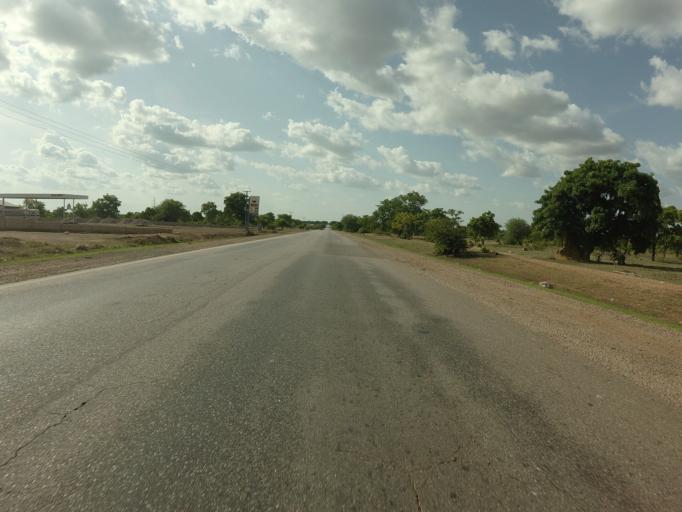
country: GH
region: Upper East
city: Bolgatanga
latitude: 10.6510
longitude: -0.8579
